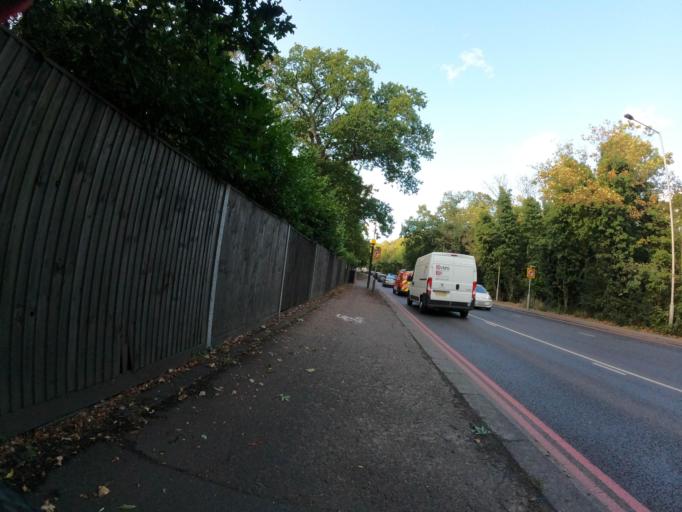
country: GB
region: England
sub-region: Greater London
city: Ealing Broadway
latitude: 51.5224
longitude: -0.2916
